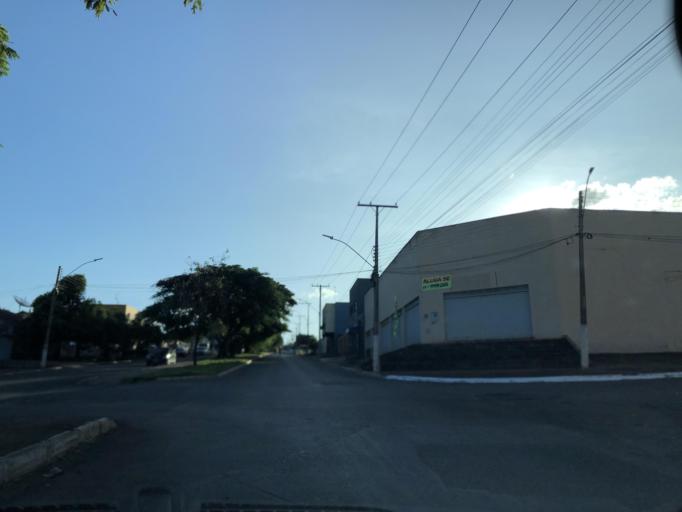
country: BR
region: Goias
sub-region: Luziania
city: Luziania
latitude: -16.2613
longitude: -47.9542
